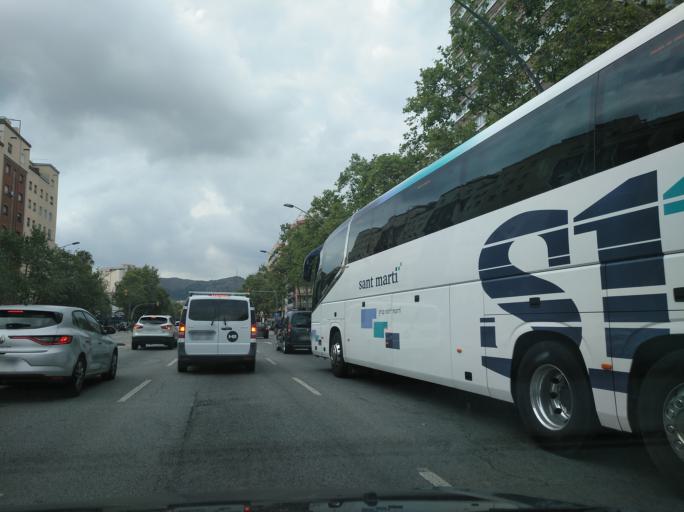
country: ES
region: Catalonia
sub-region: Provincia de Barcelona
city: Sant Andreu de Palomar
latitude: 41.4276
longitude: 2.1847
